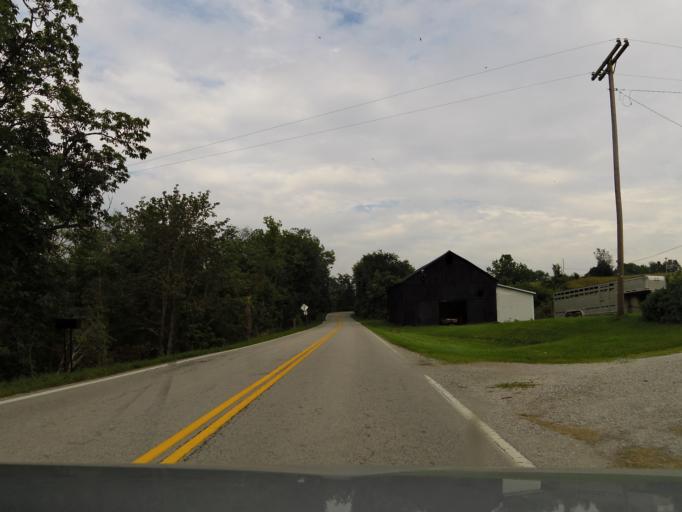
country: US
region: Kentucky
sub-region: Harrison County
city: Cynthiana
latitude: 38.4999
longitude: -84.2072
